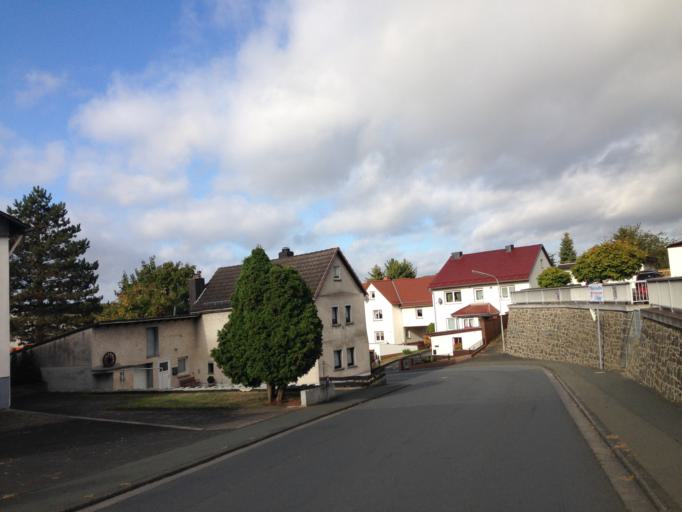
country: DE
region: Hesse
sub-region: Regierungsbezirk Giessen
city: Bad Endbach
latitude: 50.6751
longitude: 8.5274
